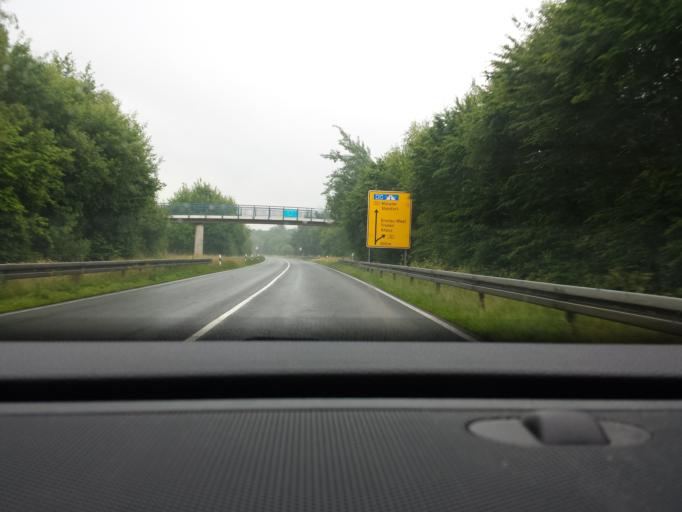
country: DE
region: North Rhine-Westphalia
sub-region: Regierungsbezirk Munster
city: Gronau
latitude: 52.1923
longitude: 6.9662
